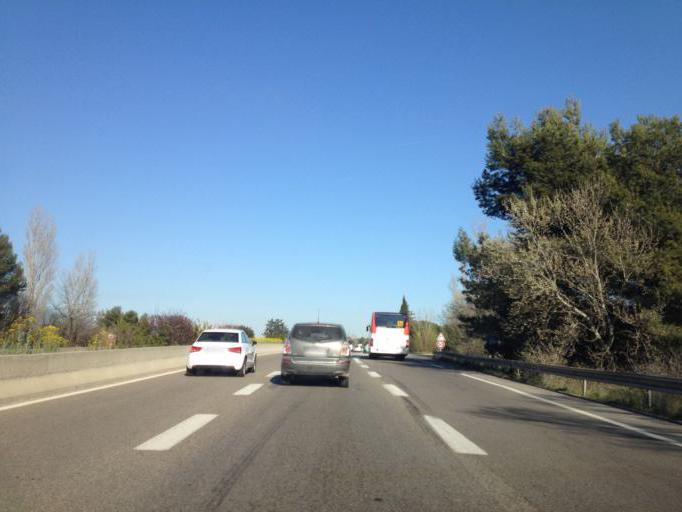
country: FR
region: Provence-Alpes-Cote d'Azur
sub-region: Departement des Bouches-du-Rhone
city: Aix-en-Provence
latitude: 43.5062
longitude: 5.4076
